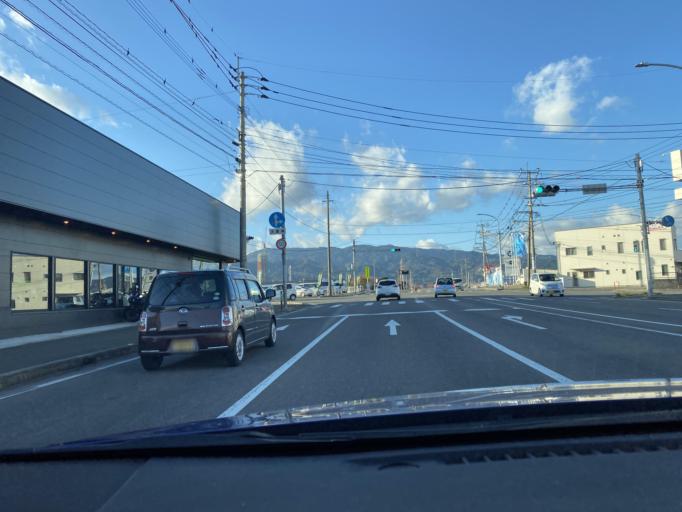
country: JP
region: Saga Prefecture
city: Tosu
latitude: 33.3598
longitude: 130.5069
